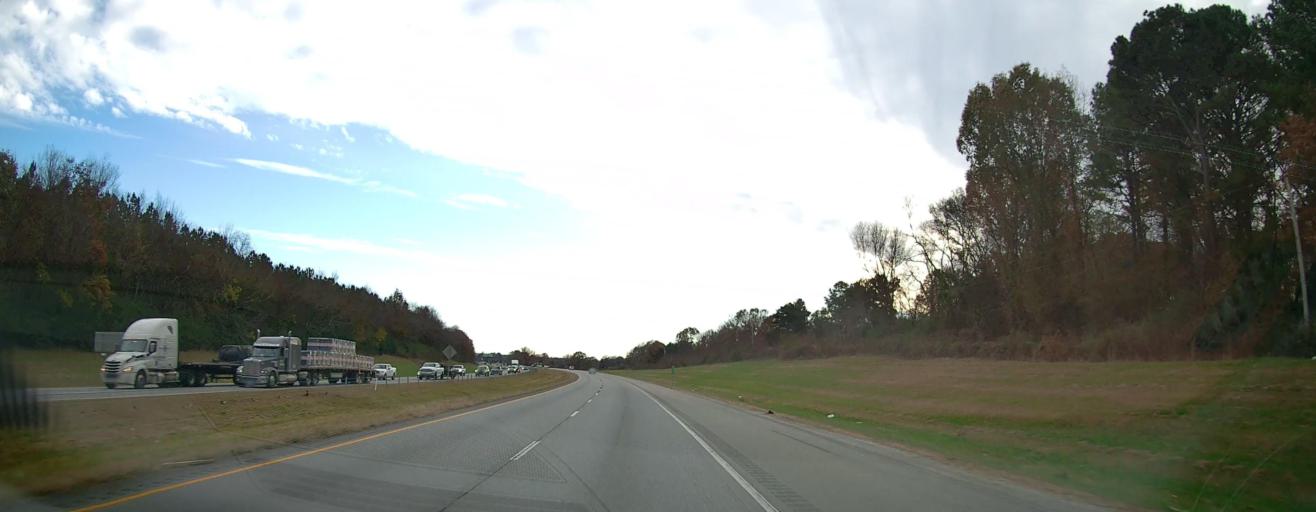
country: US
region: Alabama
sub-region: Morgan County
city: Priceville
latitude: 34.5724
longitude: -86.9102
